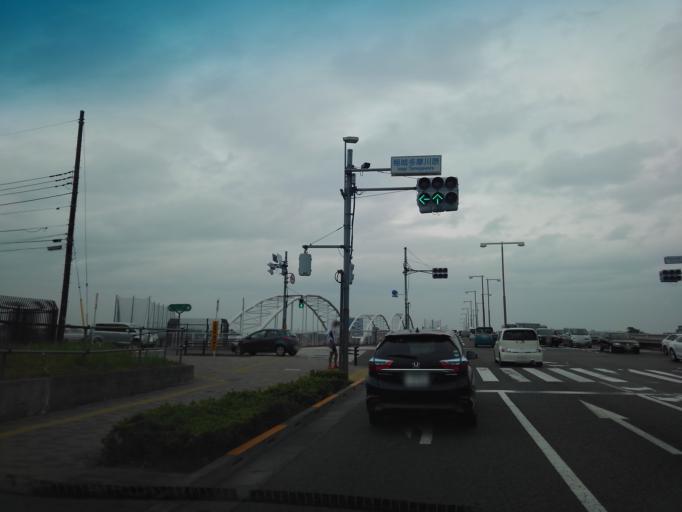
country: JP
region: Tokyo
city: Chofugaoka
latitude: 35.6423
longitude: 139.5229
